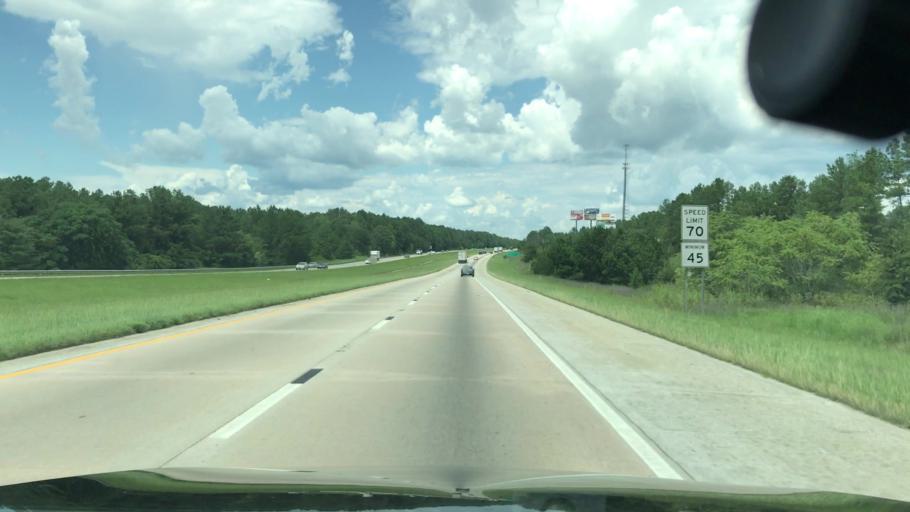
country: US
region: South Carolina
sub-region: Fairfield County
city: Winnsboro
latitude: 34.4162
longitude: -80.9955
